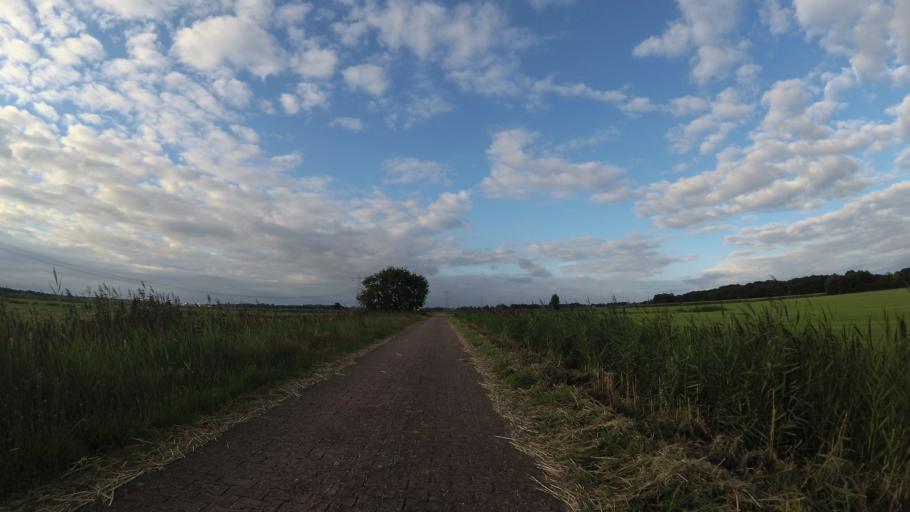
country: NL
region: North Brabant
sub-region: Gemeente Breda
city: Hoge Vucht
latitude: 51.6325
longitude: 4.7850
